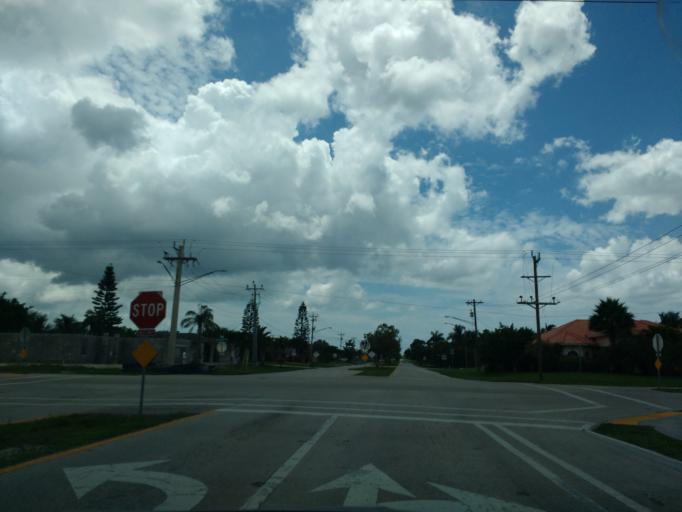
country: US
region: Florida
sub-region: Lee County
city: Cape Coral
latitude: 26.5631
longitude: -82.0173
